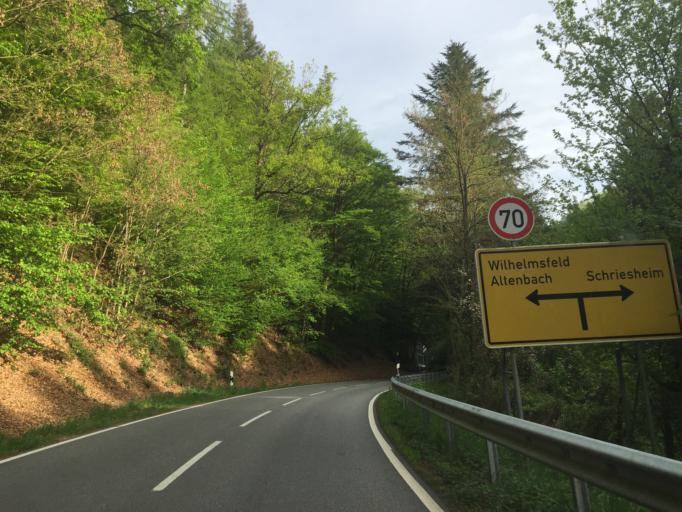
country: DE
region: Baden-Wuerttemberg
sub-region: Karlsruhe Region
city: Wilhelmsfeld
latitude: 49.4841
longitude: 8.7262
